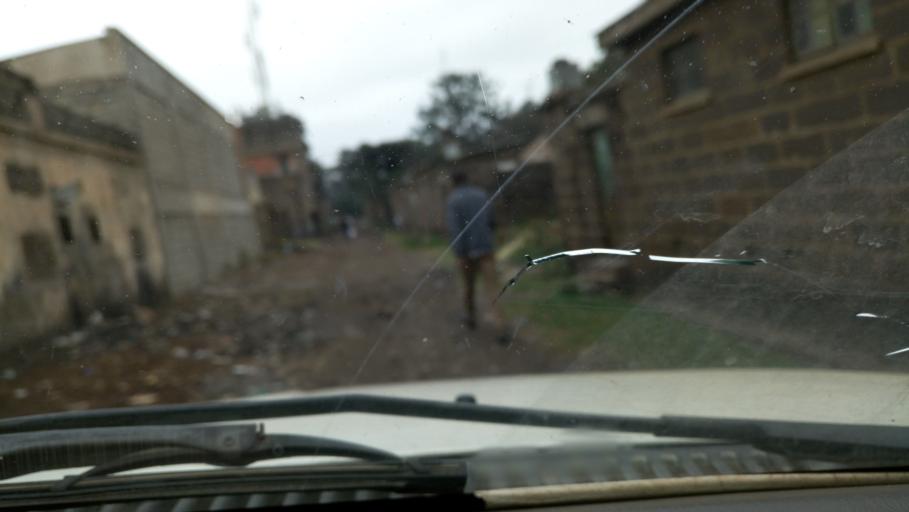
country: KE
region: Nairobi Area
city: Nairobi
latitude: -1.2743
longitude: 36.8311
